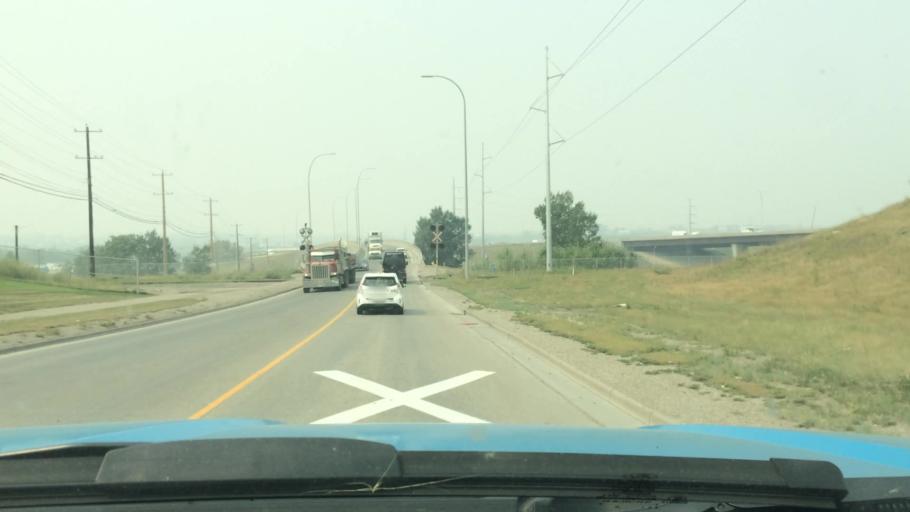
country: CA
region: Alberta
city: Calgary
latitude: 51.0088
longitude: -114.0072
